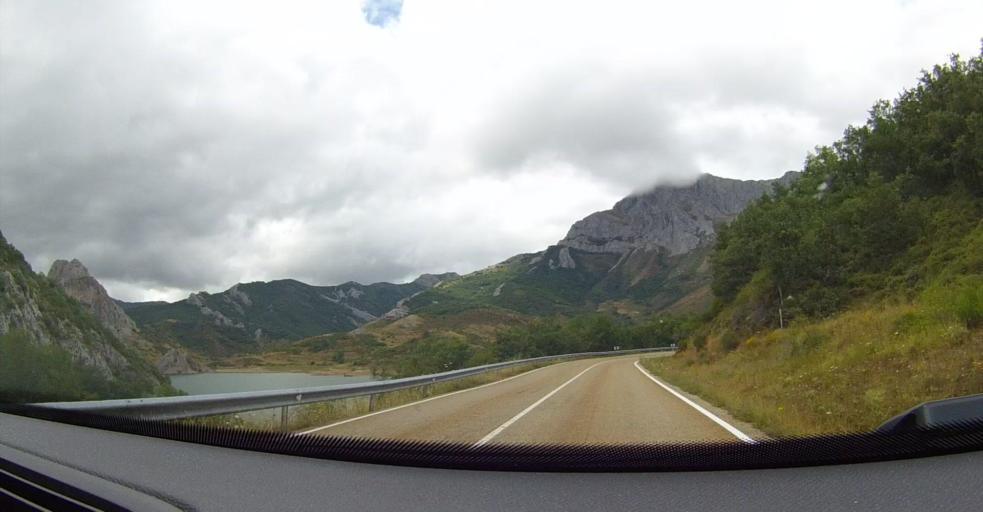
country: ES
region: Castille and Leon
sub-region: Provincia de Leon
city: Puebla de Lillo
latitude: 42.9734
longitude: -5.2589
